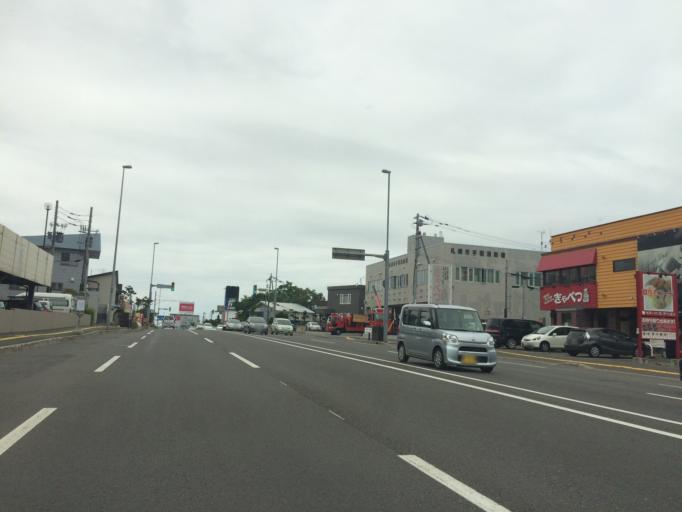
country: JP
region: Hokkaido
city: Sapporo
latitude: 43.1190
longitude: 141.2388
